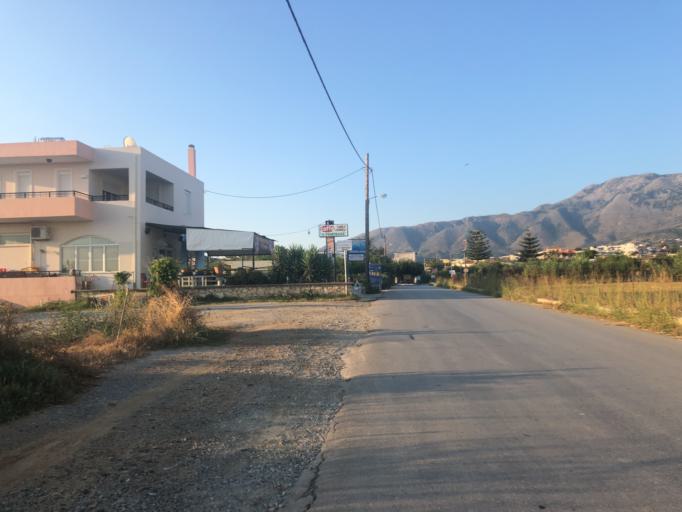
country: GR
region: Crete
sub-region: Nomos Chanias
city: Georgioupolis
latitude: 35.3490
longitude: 24.3015
